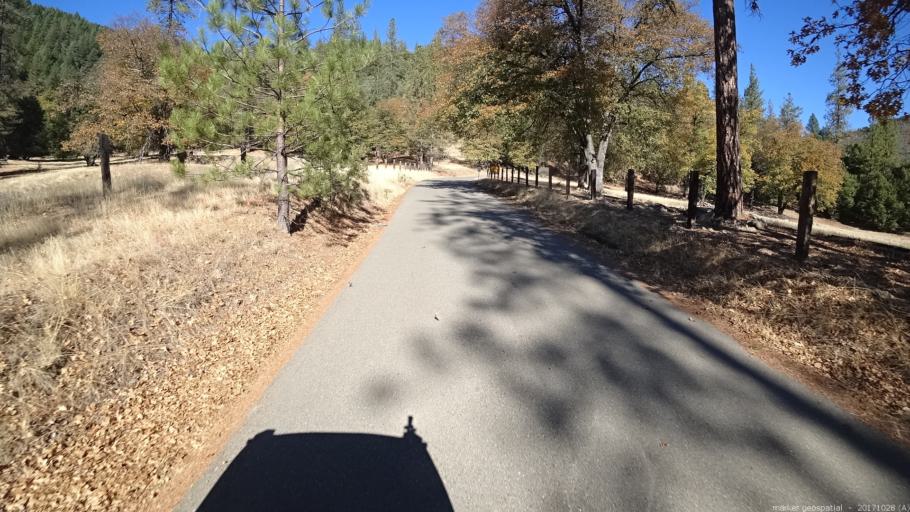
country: US
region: California
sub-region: Trinity County
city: Lewiston
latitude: 40.7916
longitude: -122.6133
